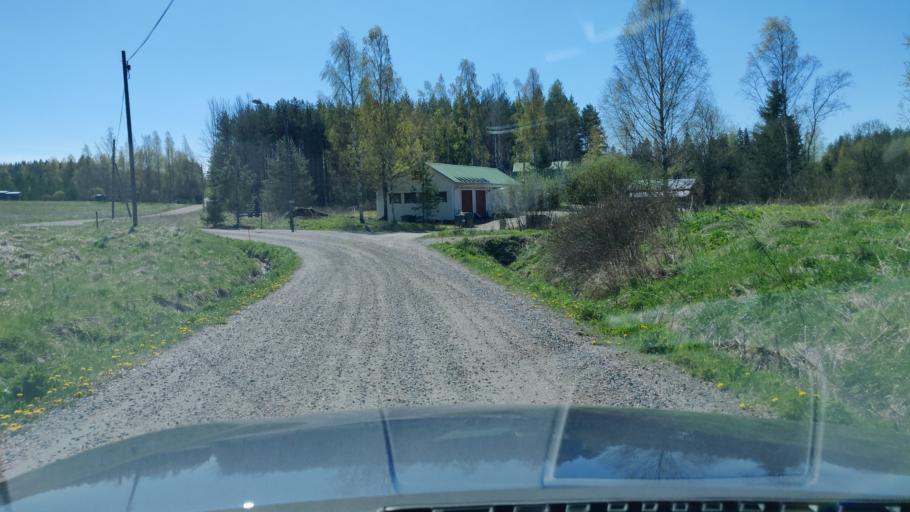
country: FI
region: Uusimaa
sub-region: Helsinki
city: Nurmijaervi
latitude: 60.3576
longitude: 24.7569
